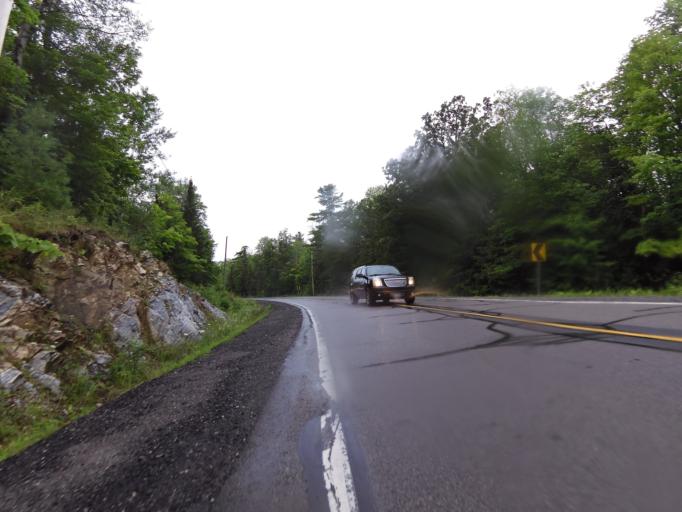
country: CA
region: Ontario
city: Perth
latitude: 44.9953
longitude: -76.3867
